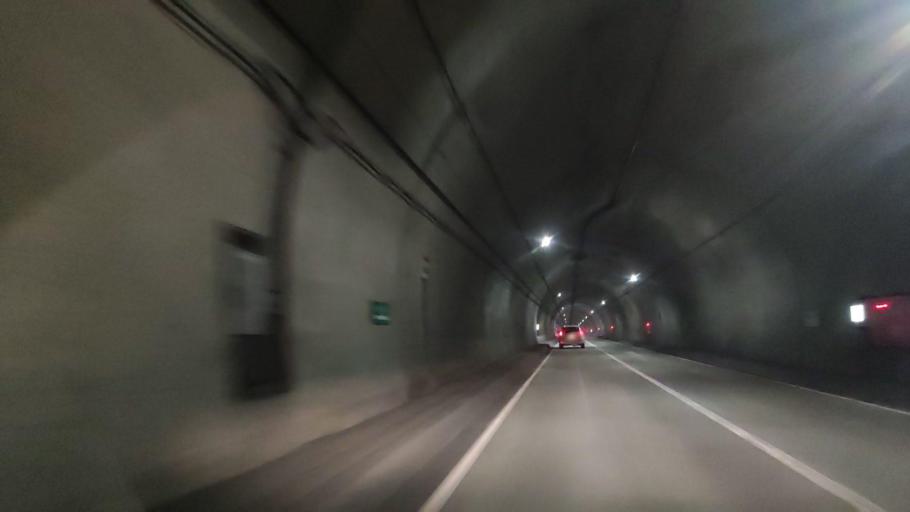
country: JP
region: Hokkaido
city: Rumoi
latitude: 43.7185
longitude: 141.3294
